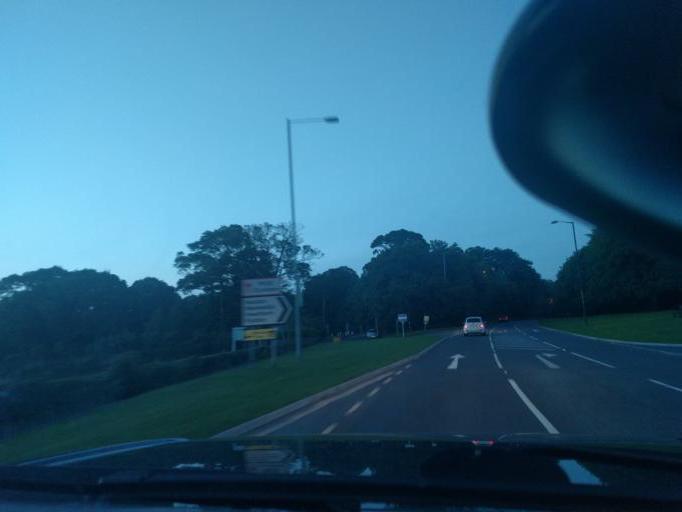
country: GB
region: England
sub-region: Wiltshire
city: Box
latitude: 51.4306
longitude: -2.2267
